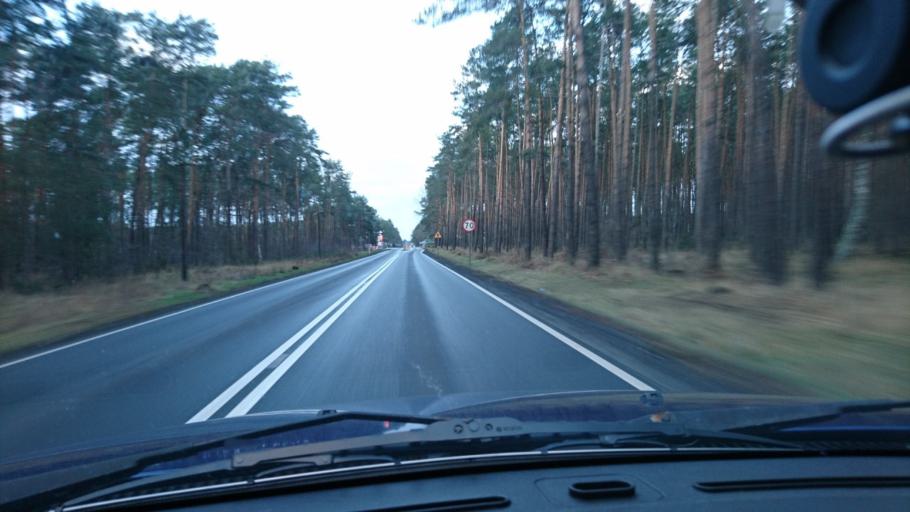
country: PL
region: Greater Poland Voivodeship
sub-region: Powiat kepinski
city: Kepno
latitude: 51.3385
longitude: 17.9533
